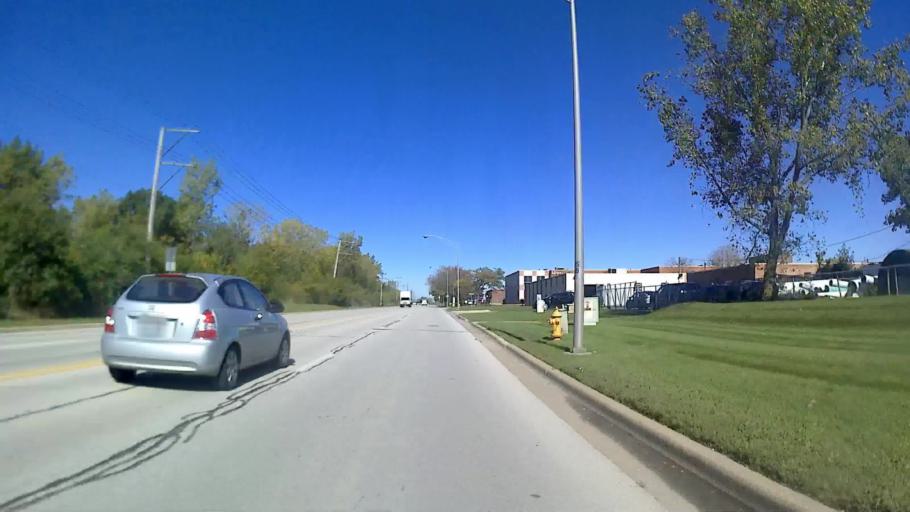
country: US
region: Illinois
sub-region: DuPage County
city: Addison
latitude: 41.9141
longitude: -88.0080
